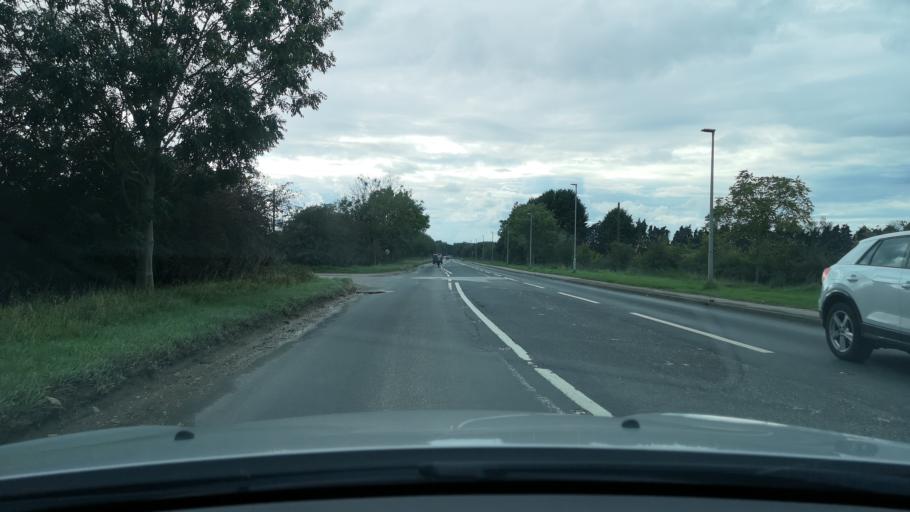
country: GB
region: England
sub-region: East Riding of Yorkshire
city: North Cave
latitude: 53.7753
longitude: -0.6639
